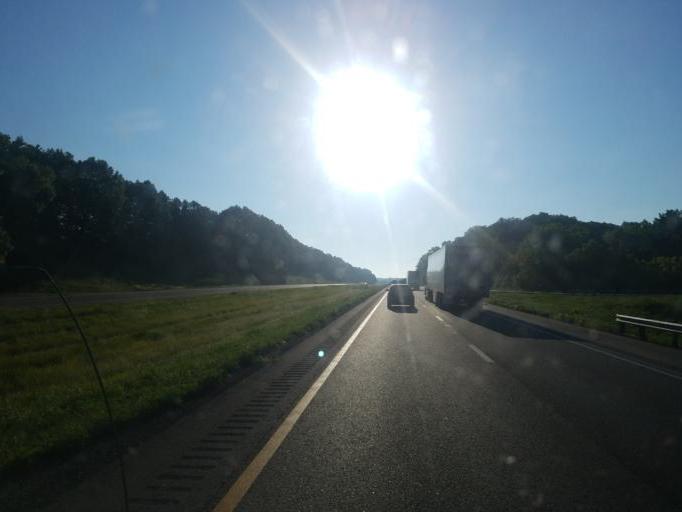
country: US
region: Illinois
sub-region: Bond County
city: Greenville
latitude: 38.9150
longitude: -89.2665
